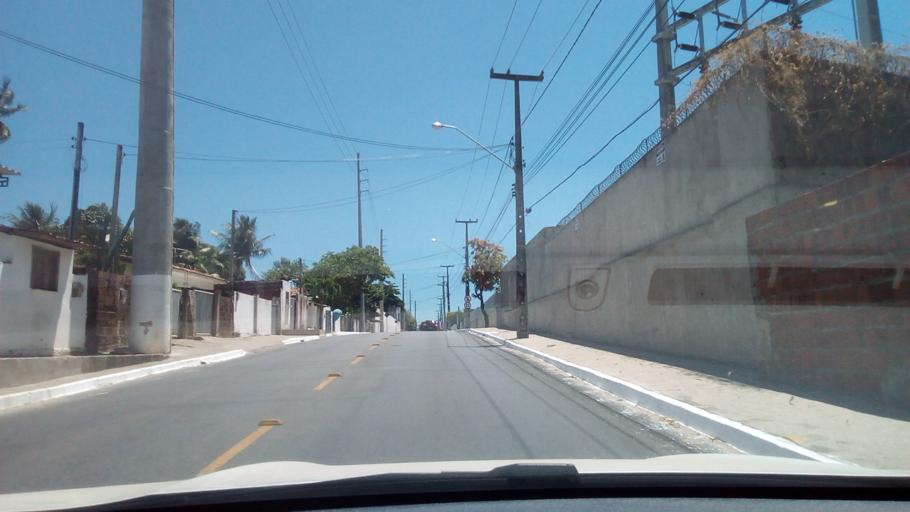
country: BR
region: Paraiba
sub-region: Joao Pessoa
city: Joao Pessoa
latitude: -7.1603
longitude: -34.8324
